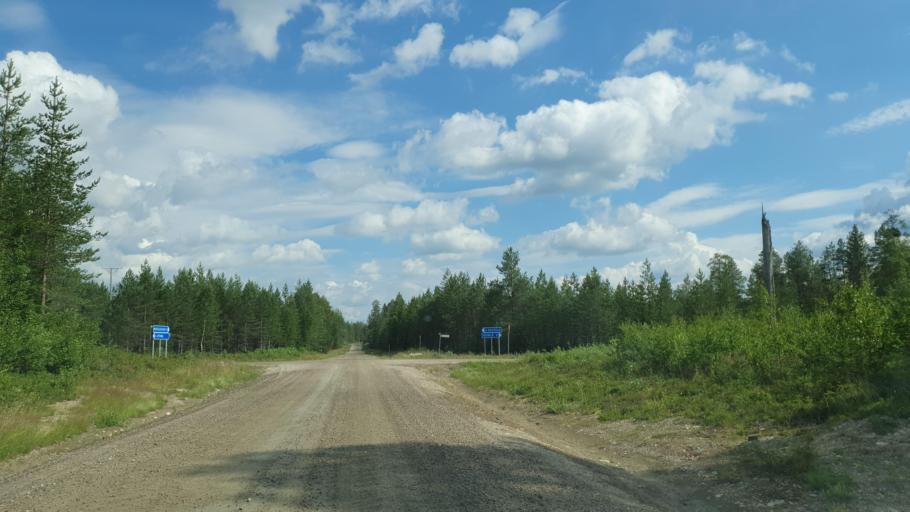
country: FI
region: Kainuu
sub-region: Kehys-Kainuu
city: Kuhmo
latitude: 64.5062
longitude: 29.6220
